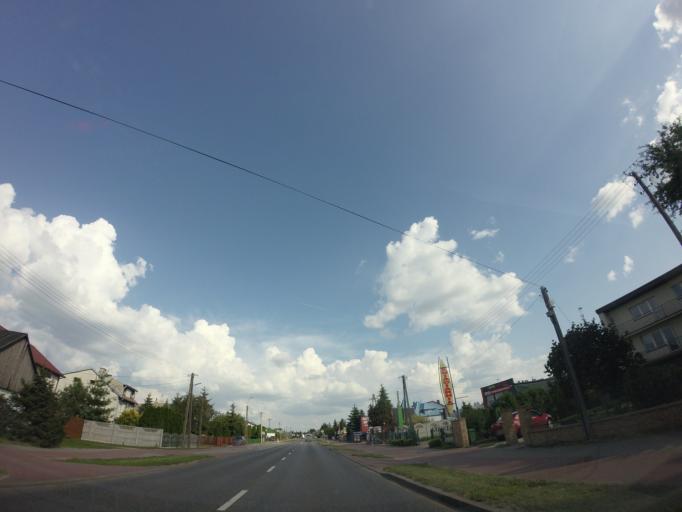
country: PL
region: Masovian Voivodeship
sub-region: Siedlce
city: Siedlce
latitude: 52.2025
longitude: 22.2492
